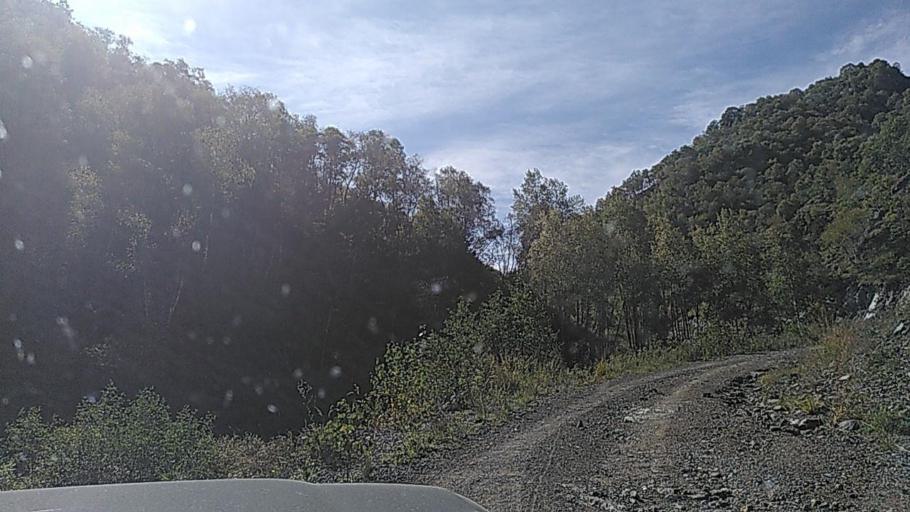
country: RU
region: Kabardino-Balkariya
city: Kamennomostskoye
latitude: 43.7141
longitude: 42.8467
